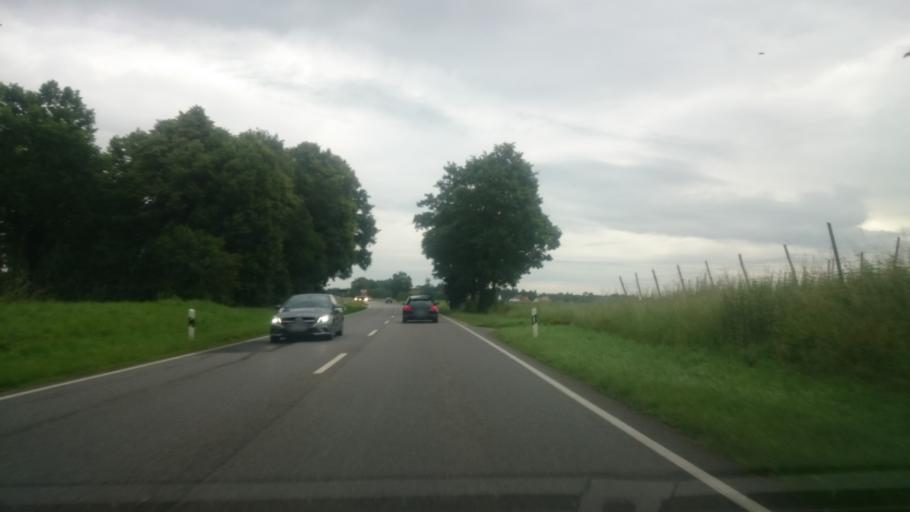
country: DE
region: Bavaria
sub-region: Upper Bavaria
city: Pornbach
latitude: 48.6045
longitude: 11.4274
